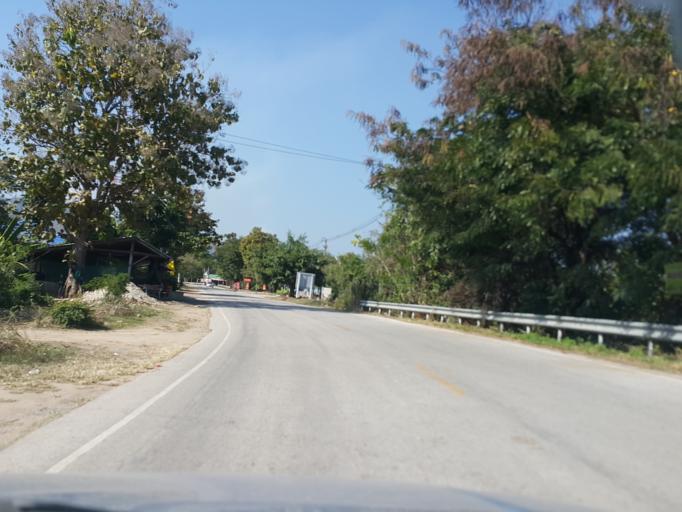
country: TH
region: Chiang Mai
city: Mae Wang
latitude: 18.6131
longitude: 98.7801
